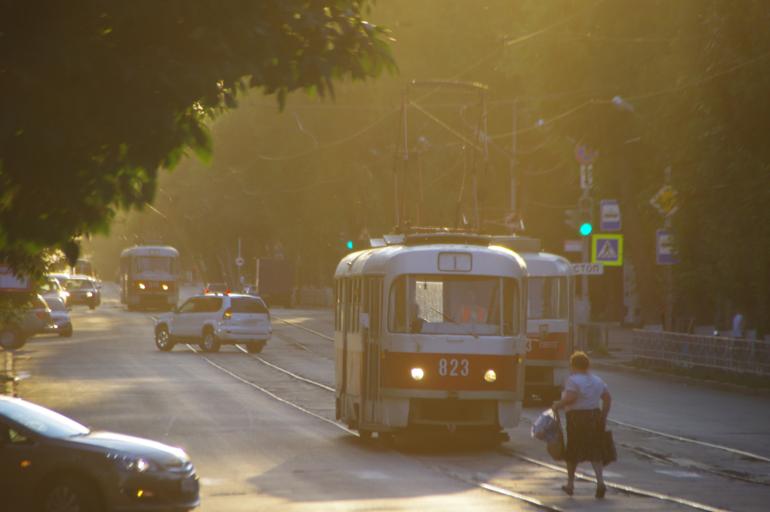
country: RU
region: Samara
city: Samara
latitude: 53.1911
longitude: 50.1104
